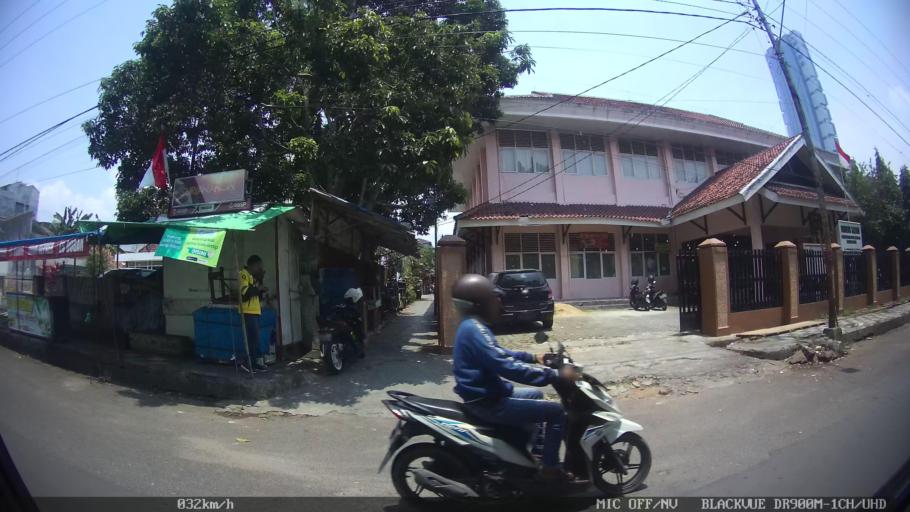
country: ID
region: Lampung
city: Bandarlampung
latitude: -5.4195
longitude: 105.2594
